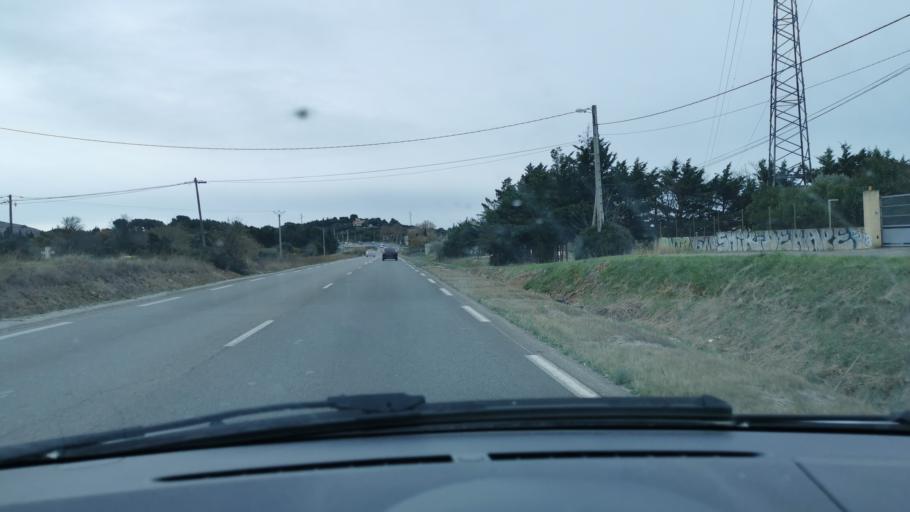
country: FR
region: Languedoc-Roussillon
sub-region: Departement de l'Herault
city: Mireval
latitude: 43.5106
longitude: 3.8007
